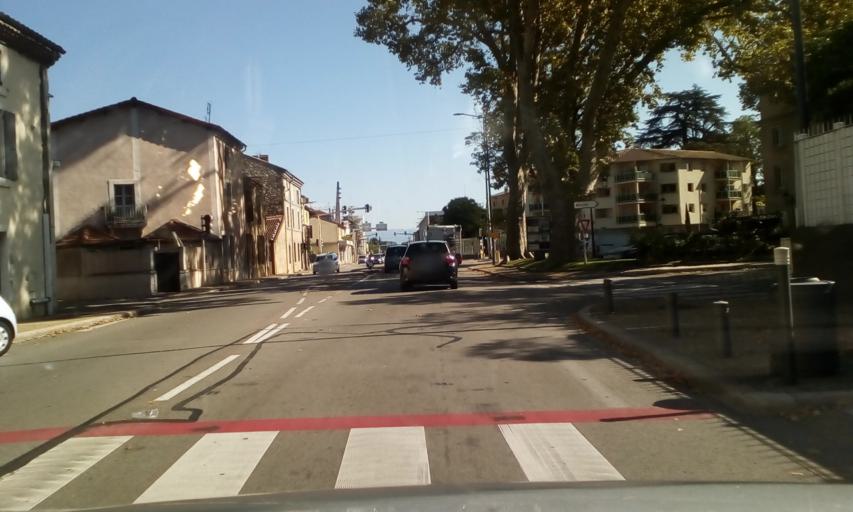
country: FR
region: Rhone-Alpes
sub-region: Departement de l'Ardeche
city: Tournon-sur-Rhone
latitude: 45.0693
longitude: 4.8411
